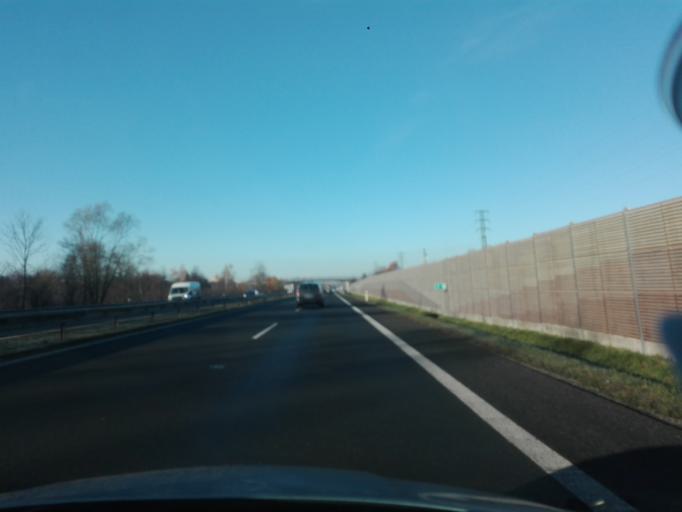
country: CZ
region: Moravskoslezsky
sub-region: Okres Frydek-Mistek
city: Stare Mesto
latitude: 49.6824
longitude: 18.3825
